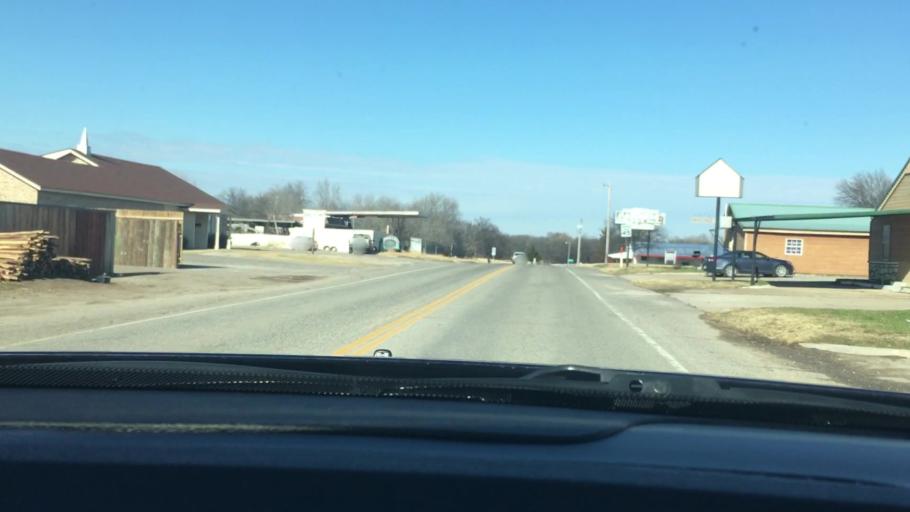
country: US
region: Oklahoma
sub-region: Murray County
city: Davis
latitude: 34.5078
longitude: -97.1211
